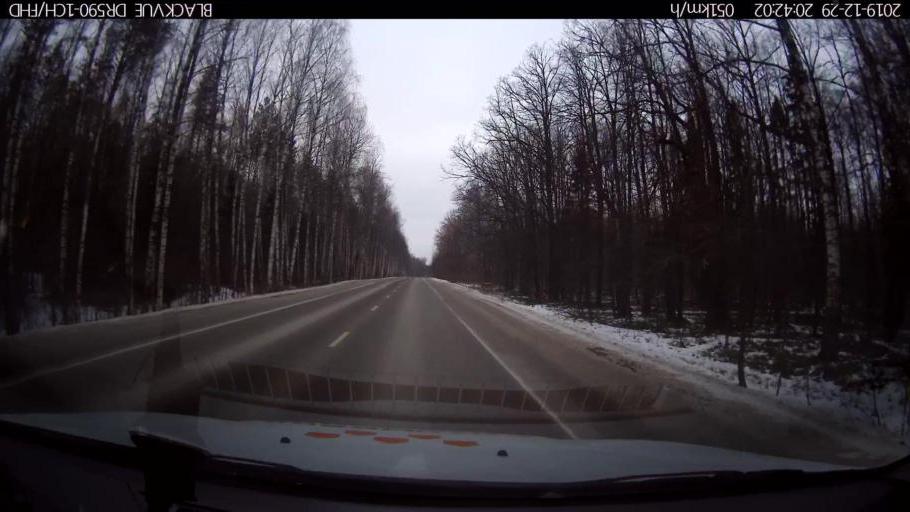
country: RU
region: Nizjnij Novgorod
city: Afonino
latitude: 56.1890
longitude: 44.0328
